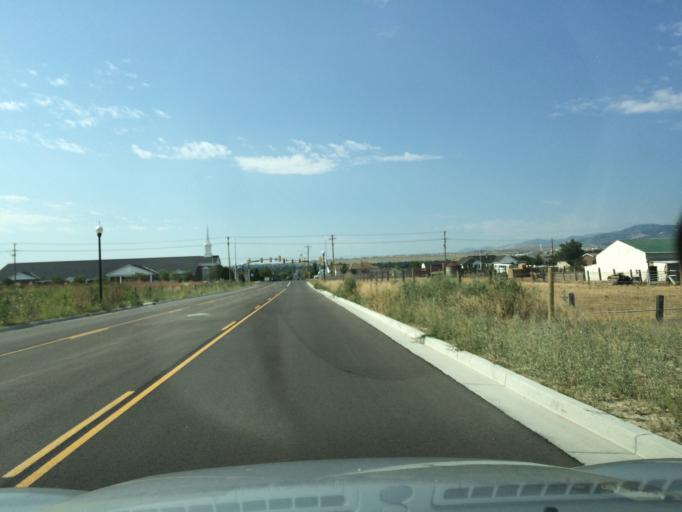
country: US
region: Utah
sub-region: Salt Lake County
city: West Valley City
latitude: 40.7114
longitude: -112.0441
